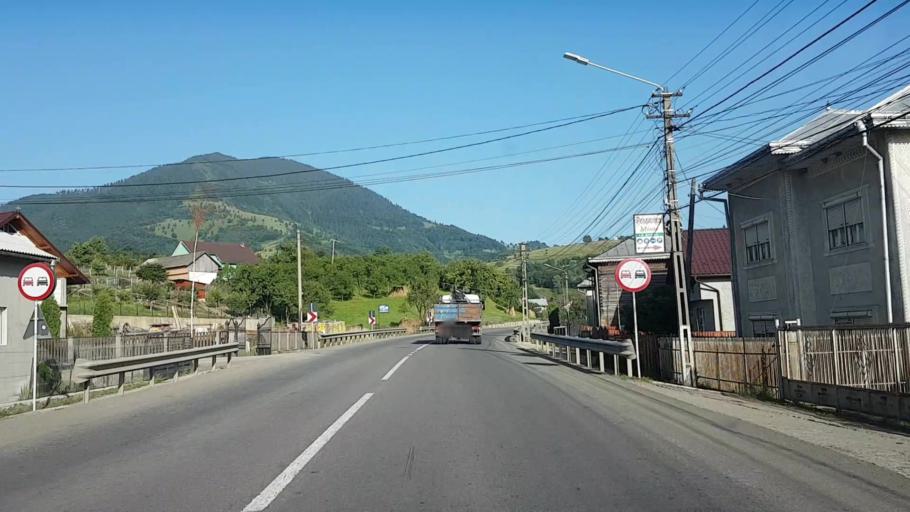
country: RO
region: Bistrita-Nasaud
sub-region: Comuna Tiha Bargaului
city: Tureac
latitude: 47.2124
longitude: 24.8528
